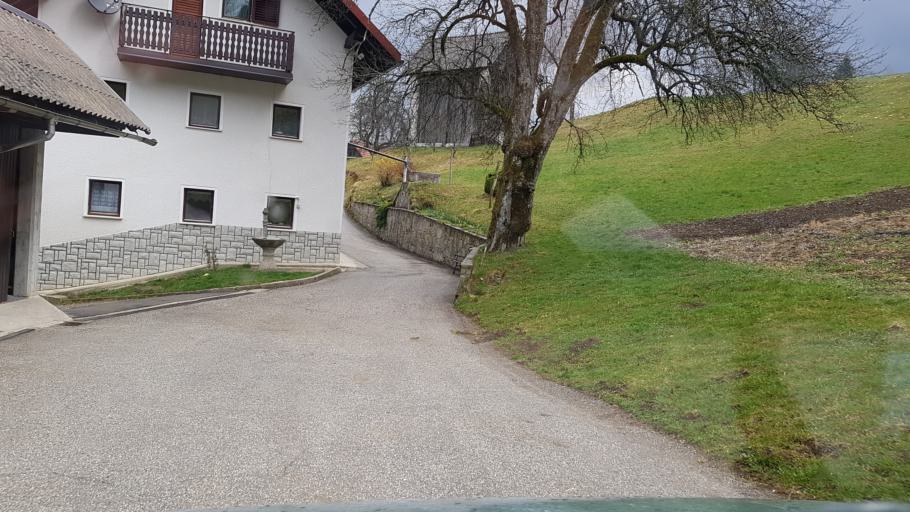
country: SI
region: Cerkno
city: Cerkno
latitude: 46.1404
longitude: 13.8807
